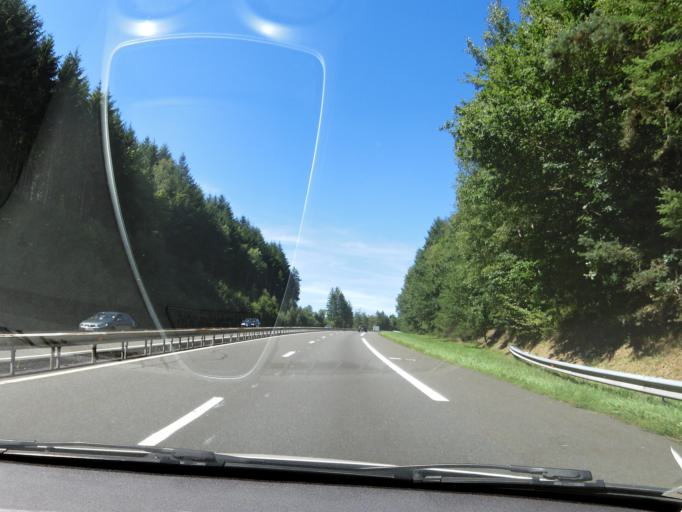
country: FR
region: Auvergne
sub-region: Departement du Puy-de-Dome
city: Celles-sur-Durolle
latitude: 45.8728
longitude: 3.6477
